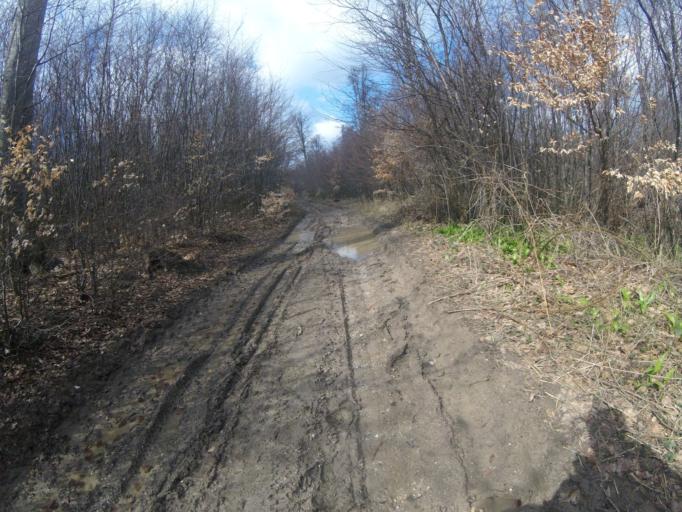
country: HU
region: Komarom-Esztergom
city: Tardos
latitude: 47.6842
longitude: 18.4978
